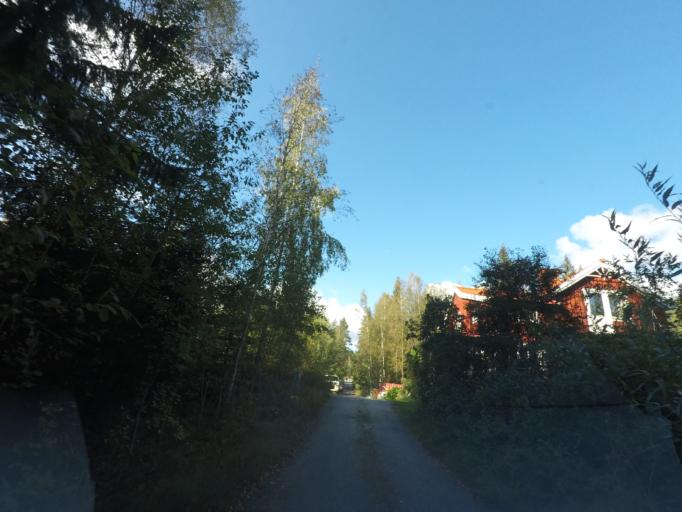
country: SE
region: Vaestmanland
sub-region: Skinnskattebergs Kommun
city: Skinnskatteberg
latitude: 59.8298
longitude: 15.5506
